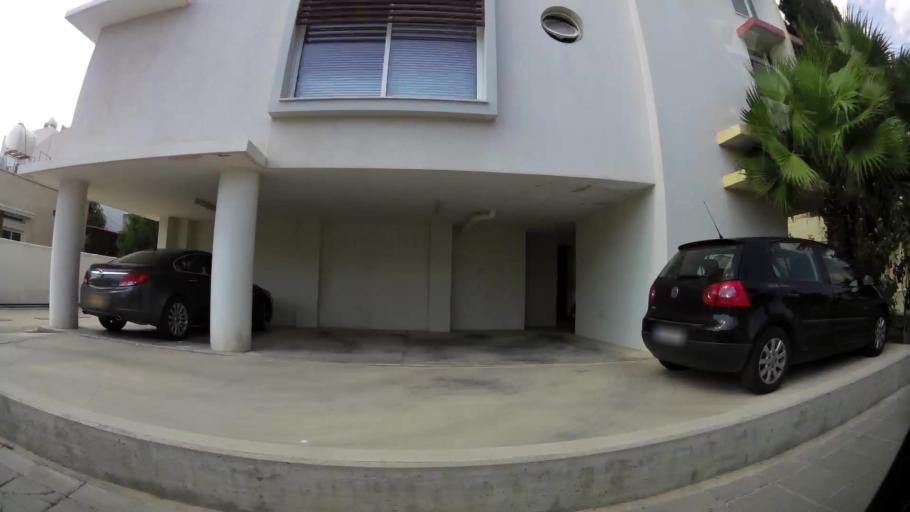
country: CY
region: Larnaka
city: Larnaca
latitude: 34.9160
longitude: 33.6235
